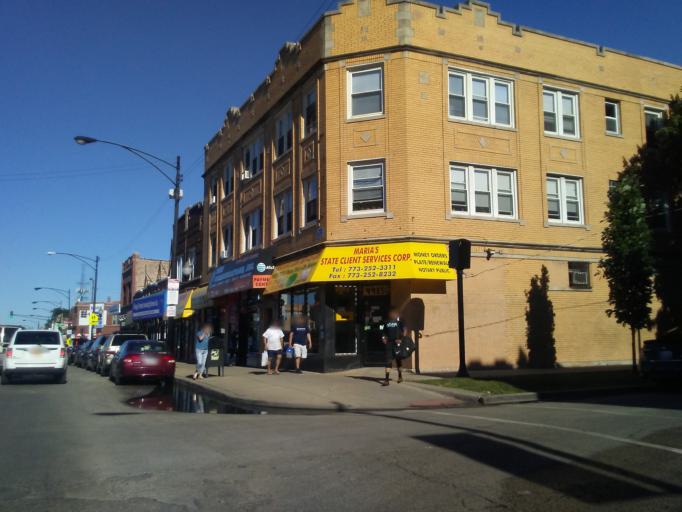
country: US
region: Illinois
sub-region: Cook County
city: Oak Park
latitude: 41.9243
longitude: -87.7379
